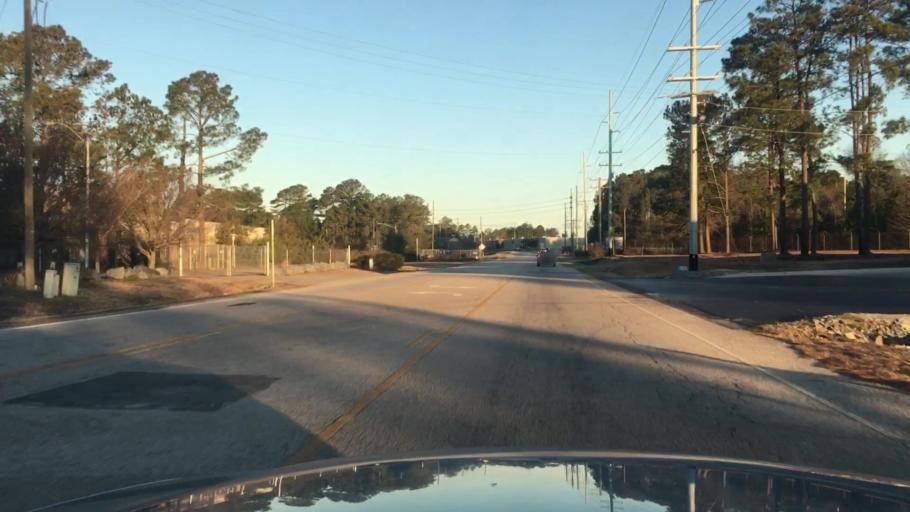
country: US
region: North Carolina
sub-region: Cumberland County
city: Hope Mills
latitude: 34.9976
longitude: -78.9029
